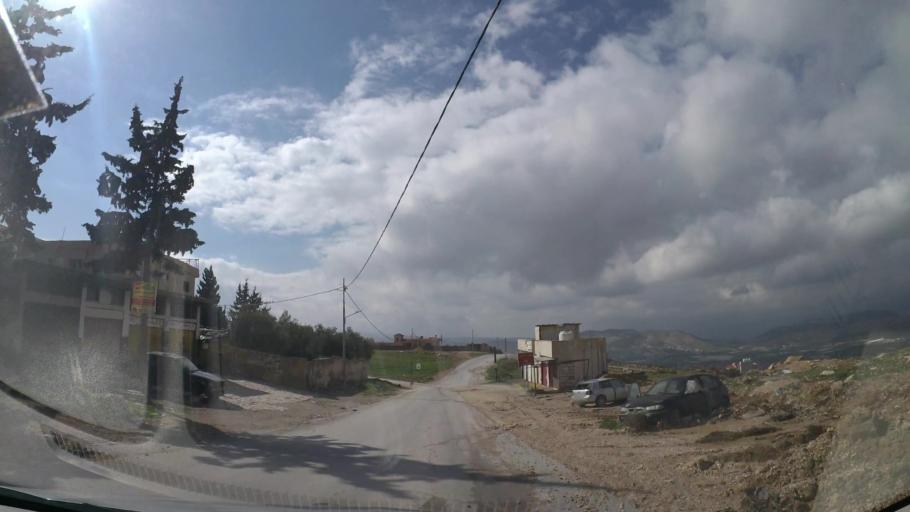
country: JO
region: Amman
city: Al Jubayhah
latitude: 32.0716
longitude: 35.8735
